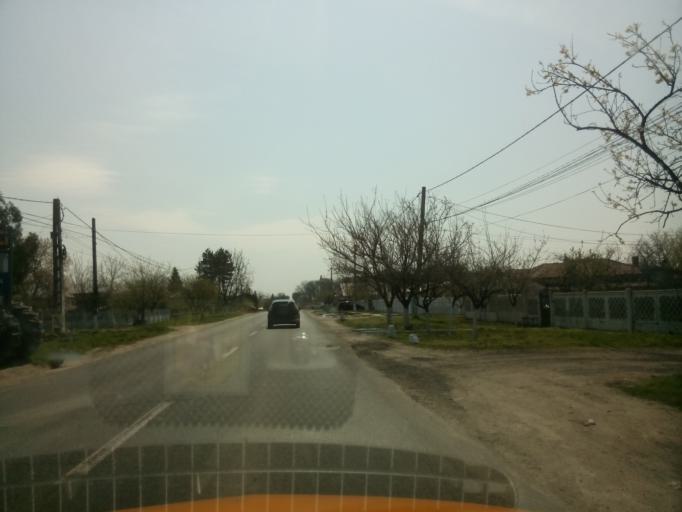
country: RO
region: Calarasi
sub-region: Comuna Frumusani
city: Frumusani
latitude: 44.2845
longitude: 26.3272
